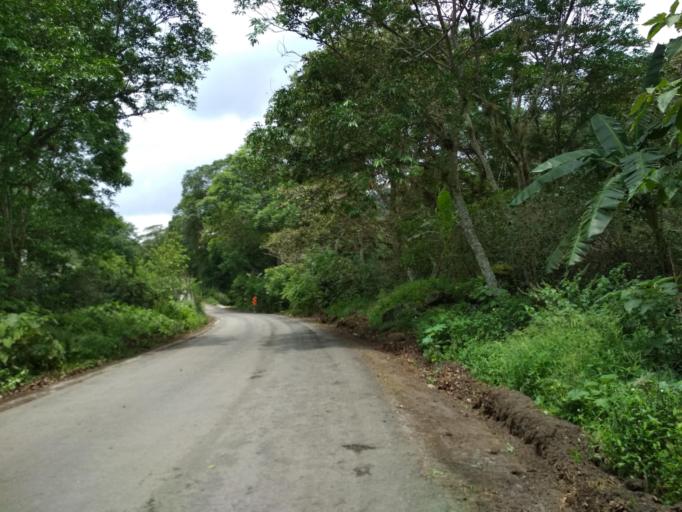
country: MX
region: Veracruz
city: Jilotepec
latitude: 19.6178
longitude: -96.9292
